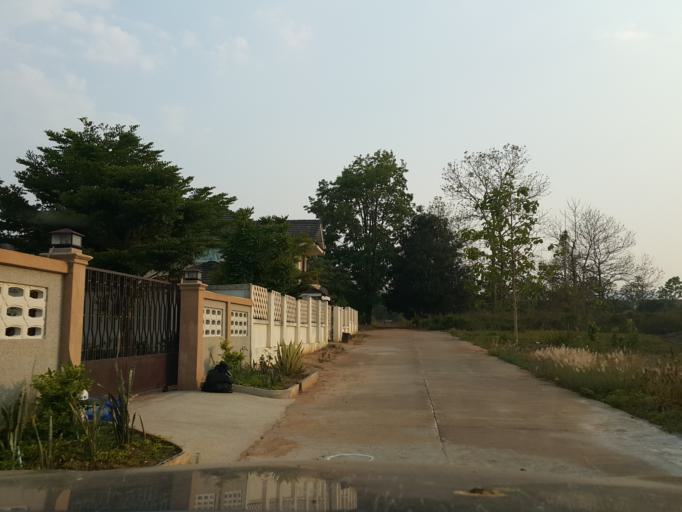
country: TH
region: Lamphun
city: Li
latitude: 17.8098
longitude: 98.9457
